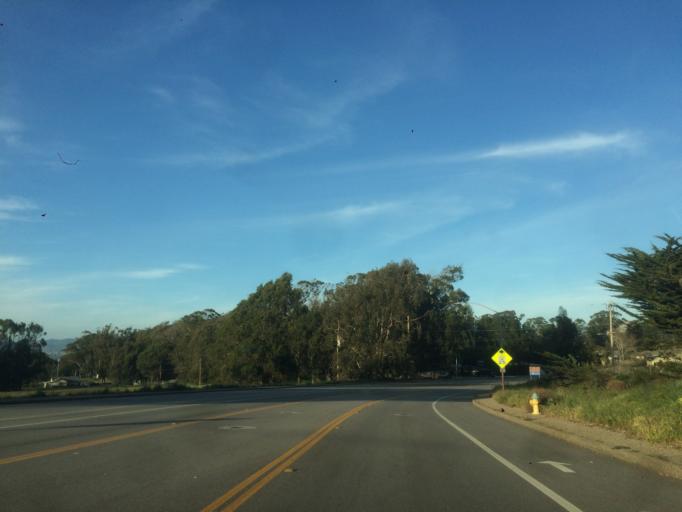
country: US
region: California
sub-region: San Luis Obispo County
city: Los Osos
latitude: 35.3119
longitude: -120.8532
